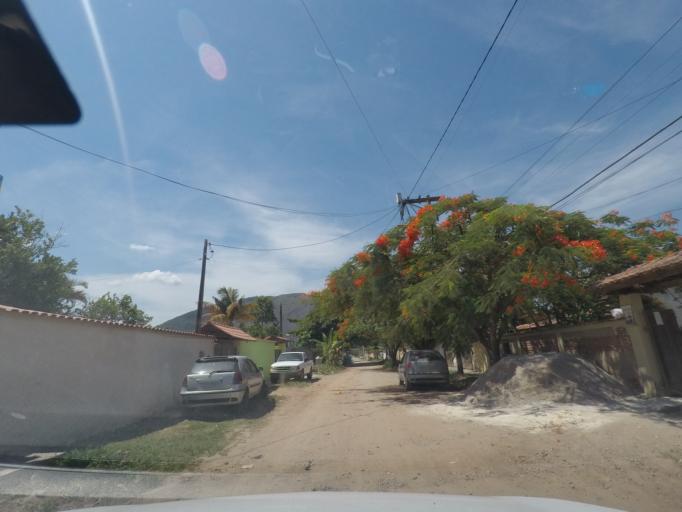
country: BR
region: Rio de Janeiro
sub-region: Marica
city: Marica
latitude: -22.9562
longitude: -42.9586
